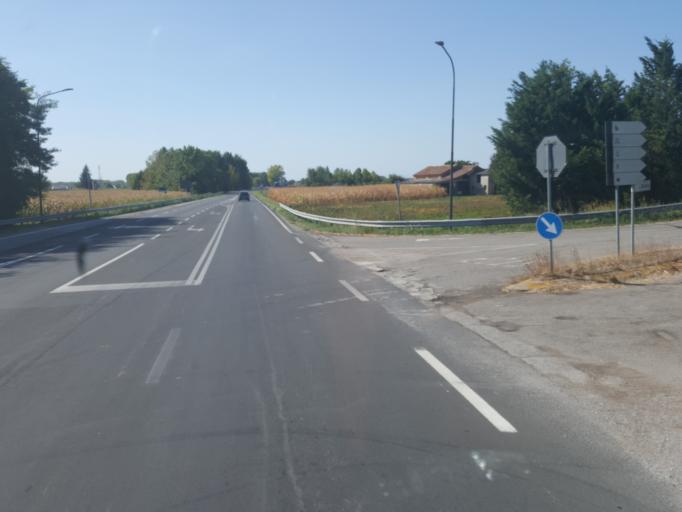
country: IT
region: Veneto
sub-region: Provincia di Rovigo
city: Castelnovo Bariano
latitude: 45.0337
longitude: 11.2992
